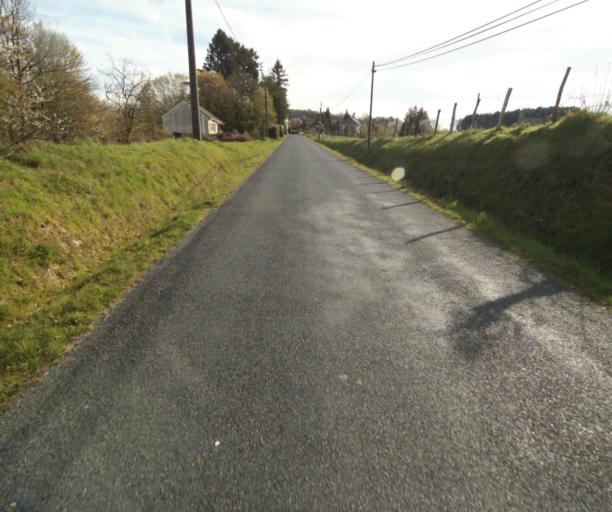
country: FR
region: Limousin
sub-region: Departement de la Correze
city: Correze
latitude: 45.3557
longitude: 1.8397
